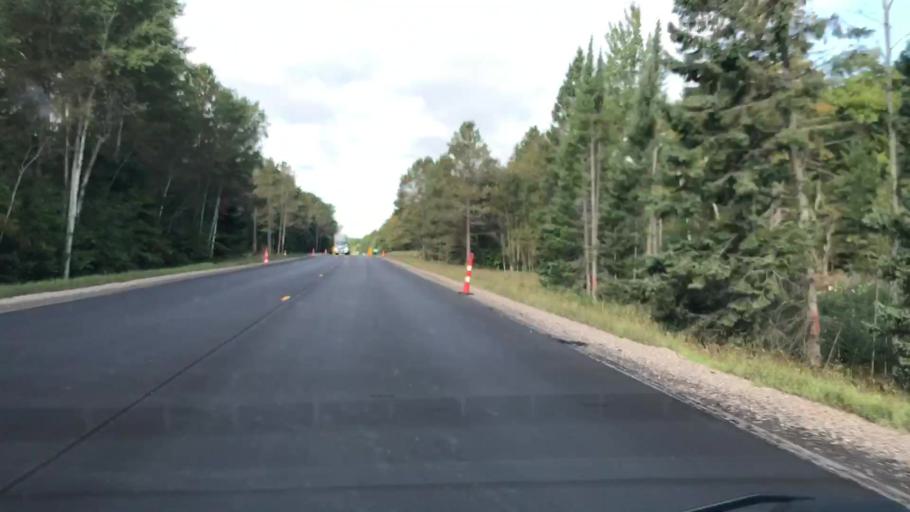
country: US
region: Michigan
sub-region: Luce County
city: Newberry
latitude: 46.3464
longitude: -85.0165
